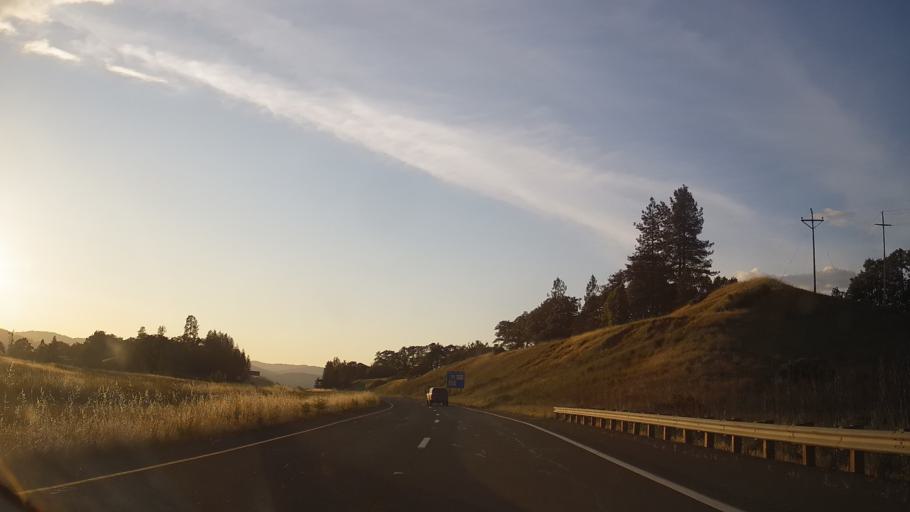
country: US
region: California
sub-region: Mendocino County
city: Willits
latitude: 39.3666
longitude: -123.3163
